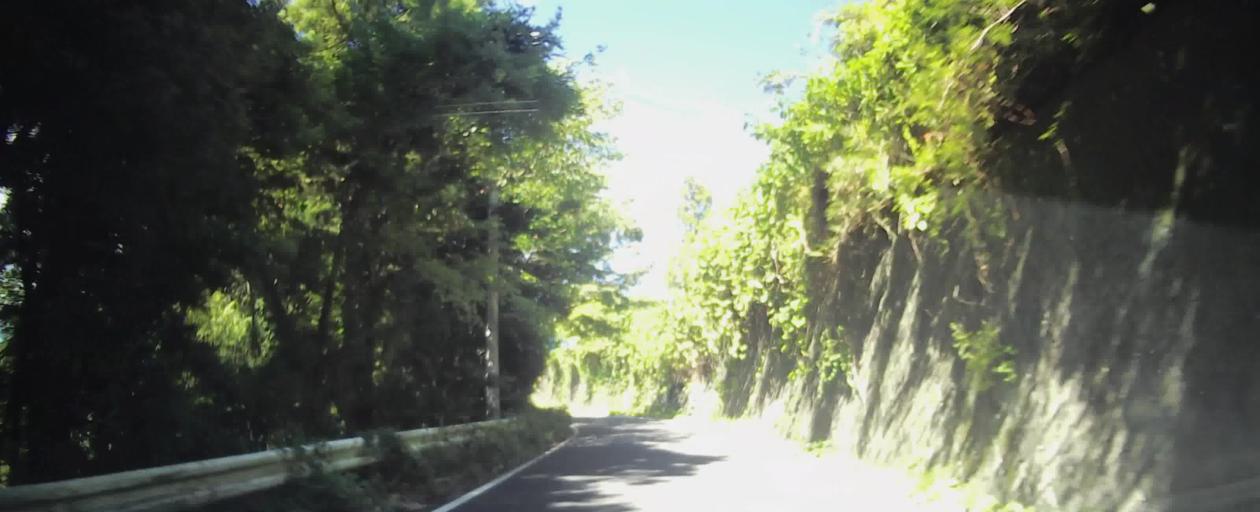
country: JP
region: Gunma
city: Kanekomachi
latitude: 36.4063
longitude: 138.9492
